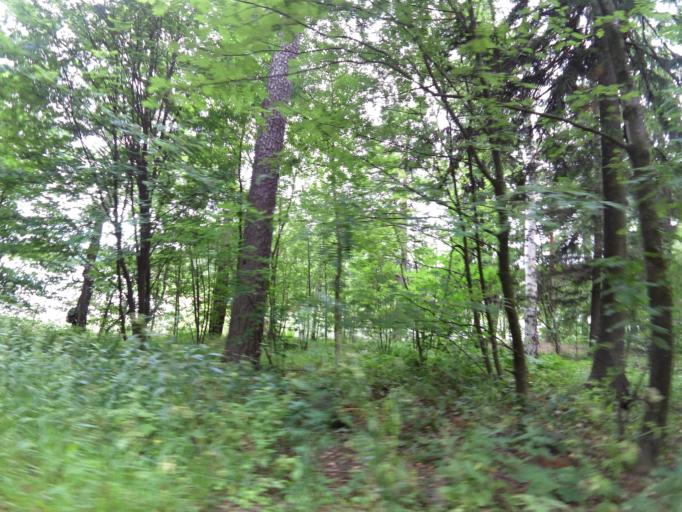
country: FI
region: Uusimaa
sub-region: Helsinki
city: Otaniemi
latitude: 60.1745
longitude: 24.8227
